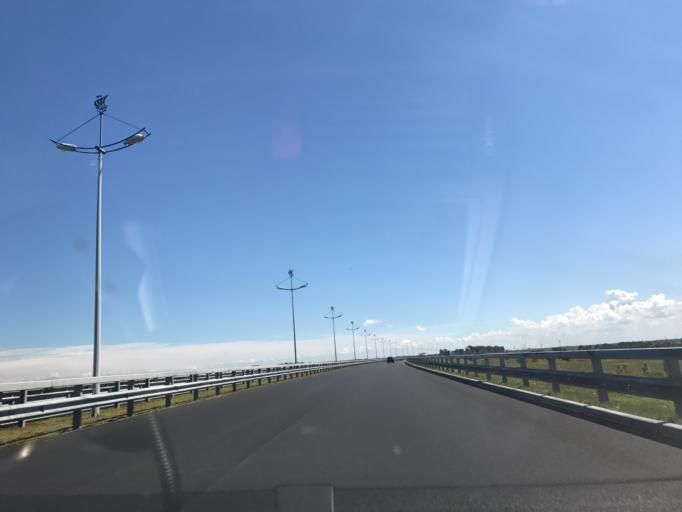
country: RU
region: Kaliningrad
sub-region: Zelenogradskiy Rayon
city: Zelenogradsk
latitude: 54.9174
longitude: 20.4792
